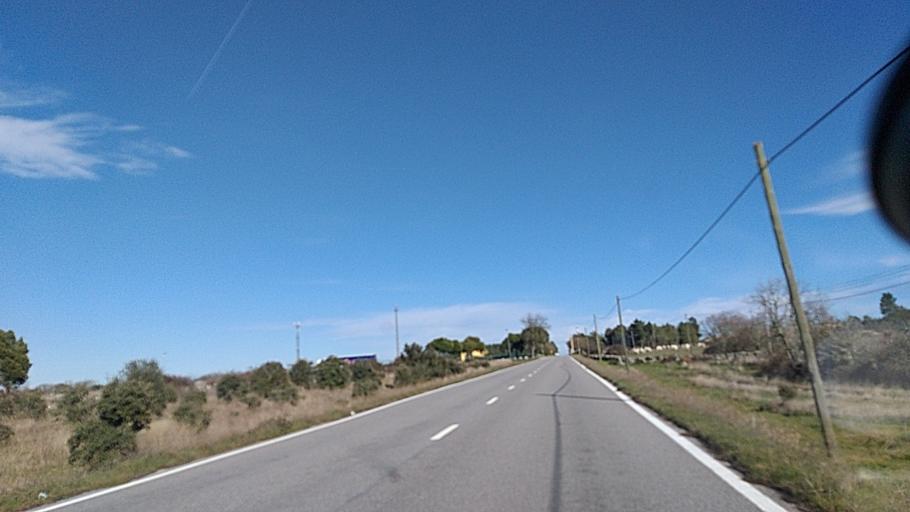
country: ES
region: Castille and Leon
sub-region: Provincia de Salamanca
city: Fuentes de Onoro
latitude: 40.6159
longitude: -6.8627
